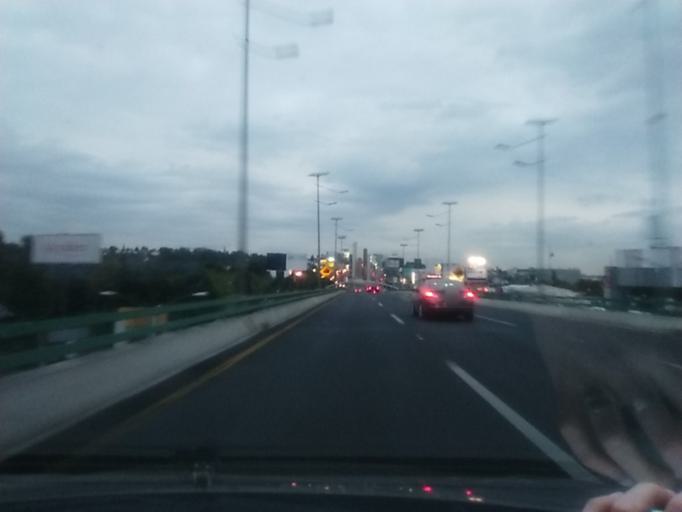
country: MX
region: Mexico
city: Naucalpan de Juarez
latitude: 19.4917
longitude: -99.2370
